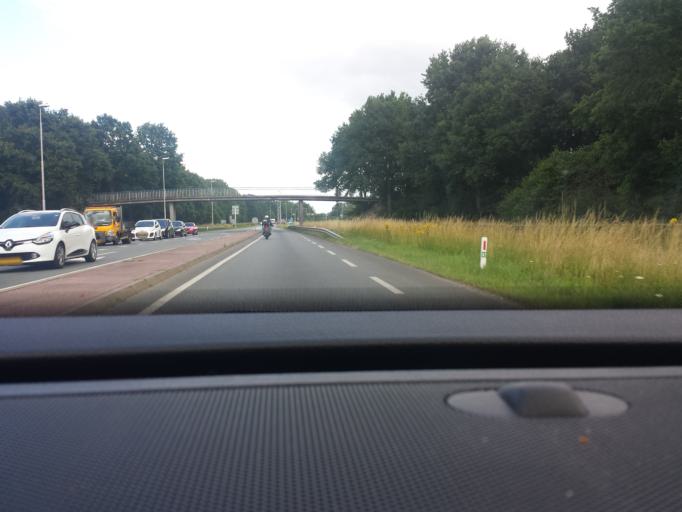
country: NL
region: Gelderland
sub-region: Gemeente Zutphen
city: Warnsveld
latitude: 52.1382
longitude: 6.2183
